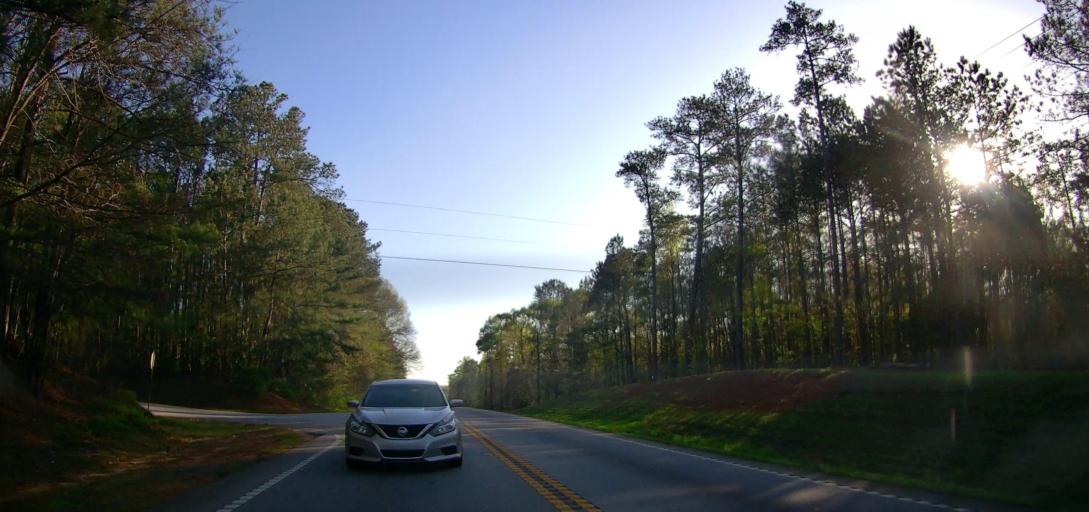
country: US
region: Georgia
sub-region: Butts County
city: Jackson
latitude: 33.4030
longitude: -83.8878
